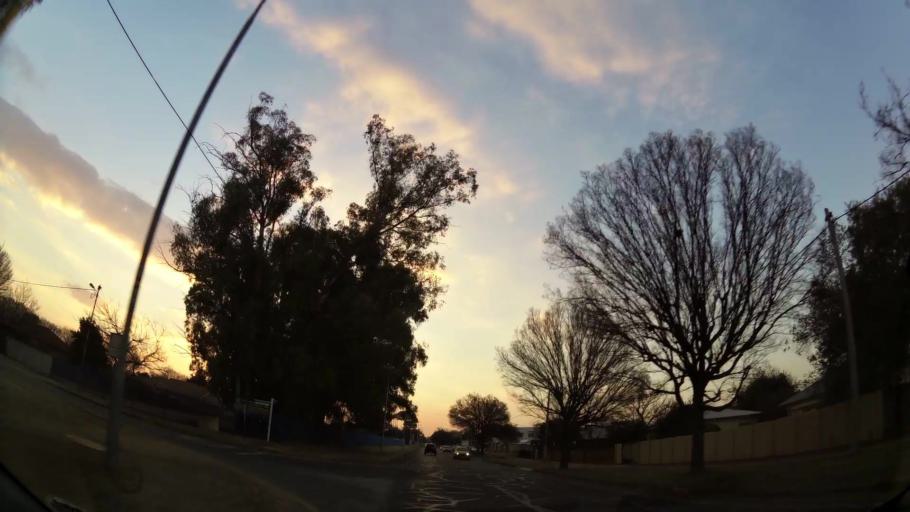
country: ZA
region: Gauteng
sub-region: Ekurhuleni Metropolitan Municipality
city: Benoni
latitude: -26.1684
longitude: 28.3159
